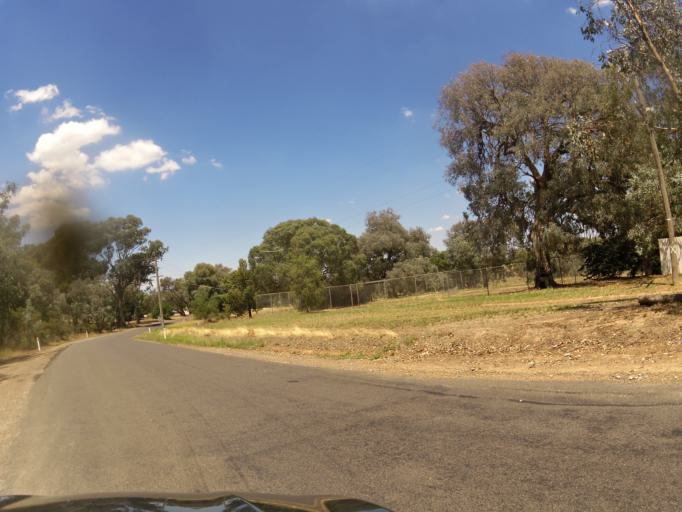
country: AU
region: Victoria
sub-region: Wangaratta
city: Wangaratta
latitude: -36.4081
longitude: 146.5470
